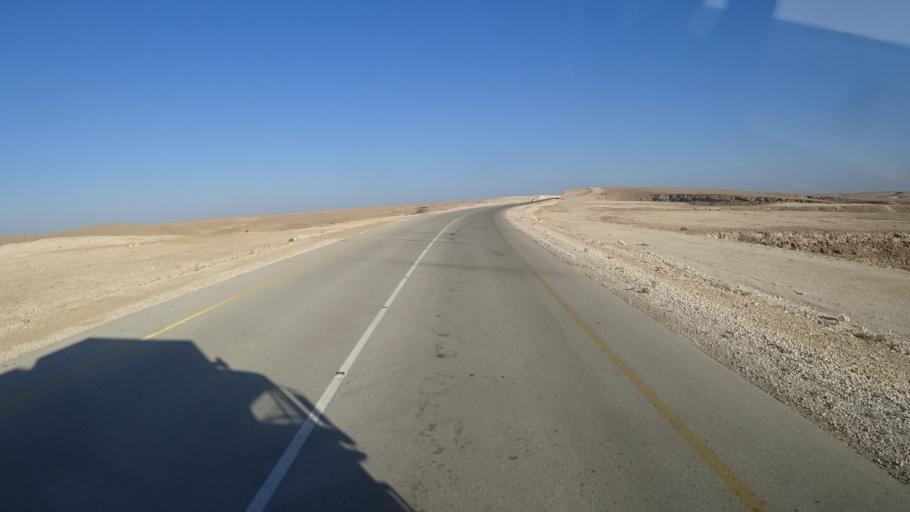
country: YE
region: Al Mahrah
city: Hawf
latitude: 17.0866
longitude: 53.0765
